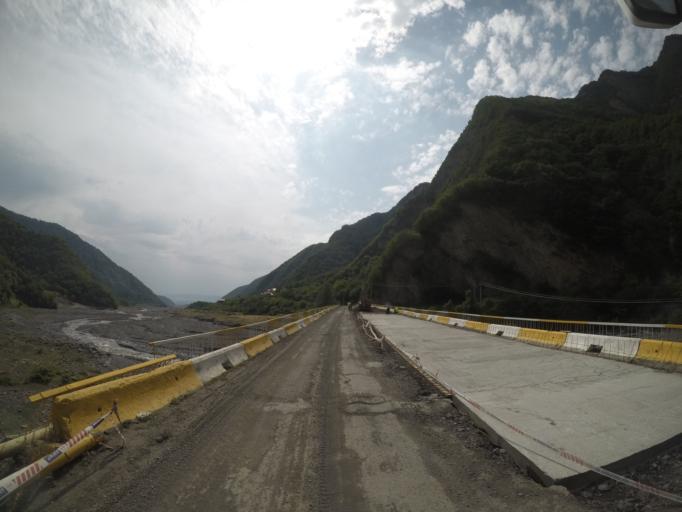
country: AZ
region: Qakh Rayon
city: Qaxbas
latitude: 41.4574
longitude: 47.0229
